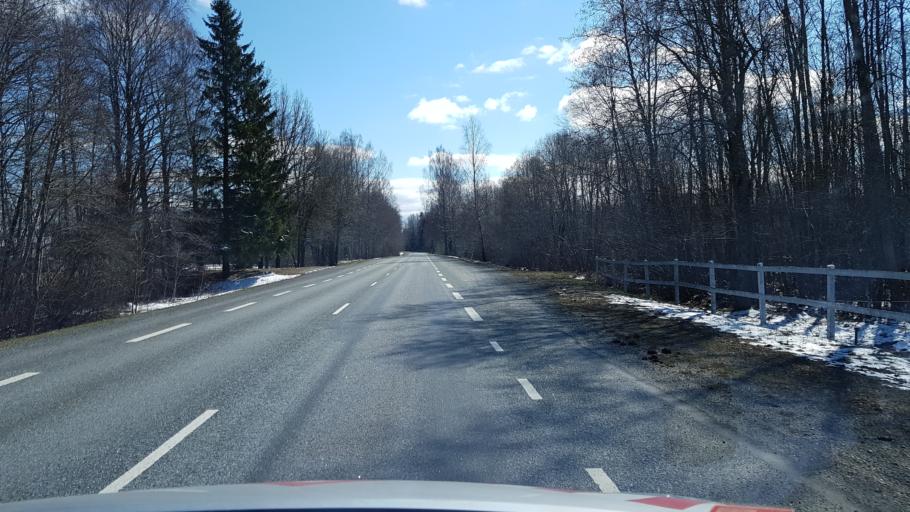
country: EE
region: Laeaene-Virumaa
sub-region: Tapa vald
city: Tapa
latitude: 59.4404
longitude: 25.9569
